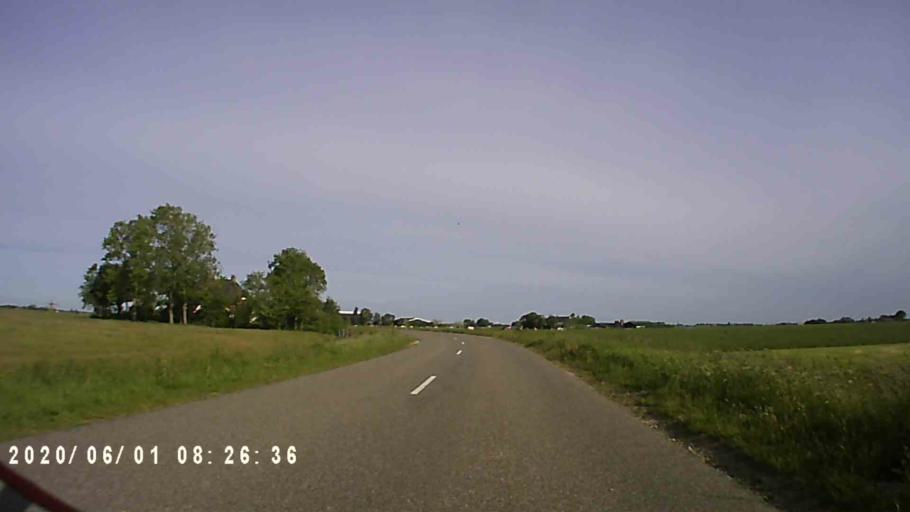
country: NL
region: Friesland
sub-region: Gemeente Ferwerderadiel
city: Burdaard
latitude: 53.2992
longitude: 5.8608
